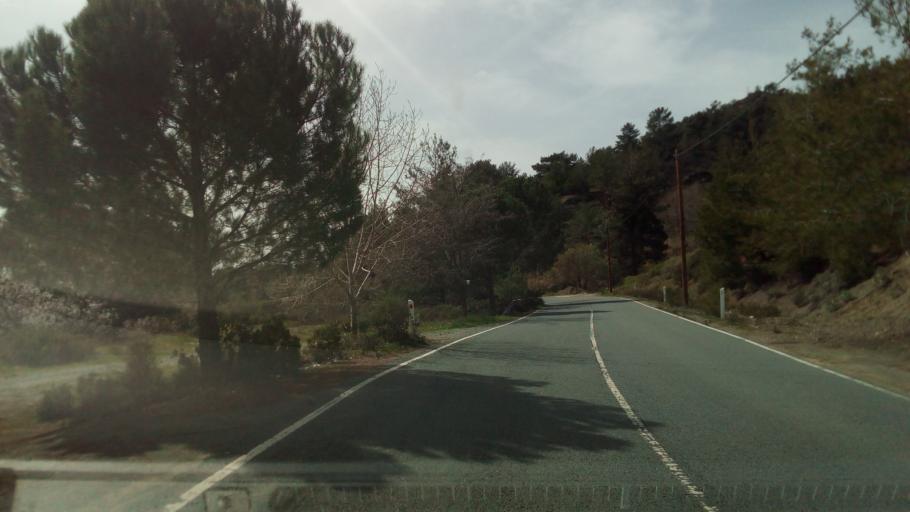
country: CY
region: Limassol
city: Pelendri
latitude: 34.9006
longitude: 32.9855
